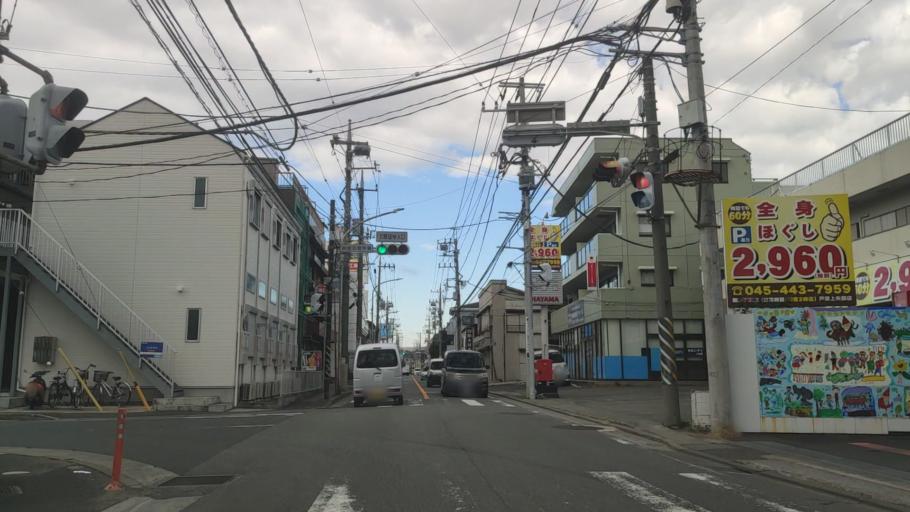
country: JP
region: Kanagawa
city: Fujisawa
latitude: 35.4222
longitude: 139.5332
